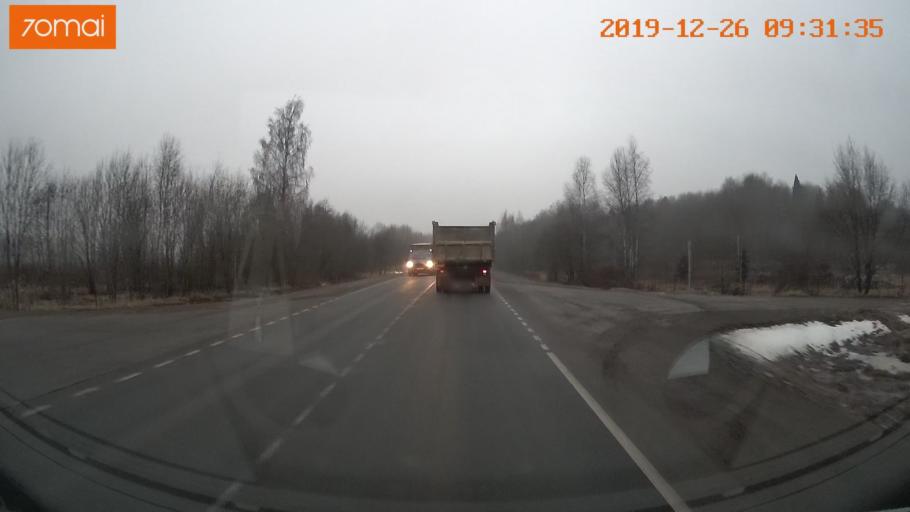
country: RU
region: Vologda
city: Gryazovets
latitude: 59.0703
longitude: 40.1264
